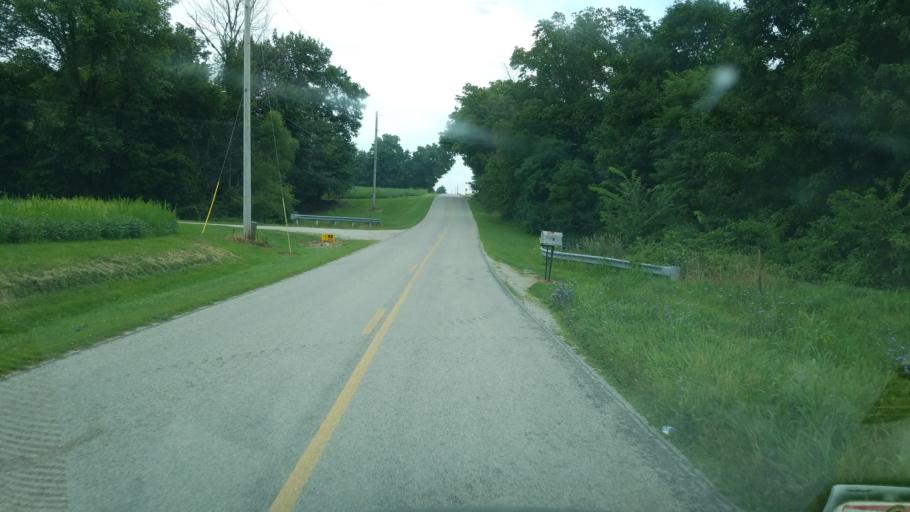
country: US
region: Ohio
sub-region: Seneca County
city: Tiffin
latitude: 41.0181
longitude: -83.0546
